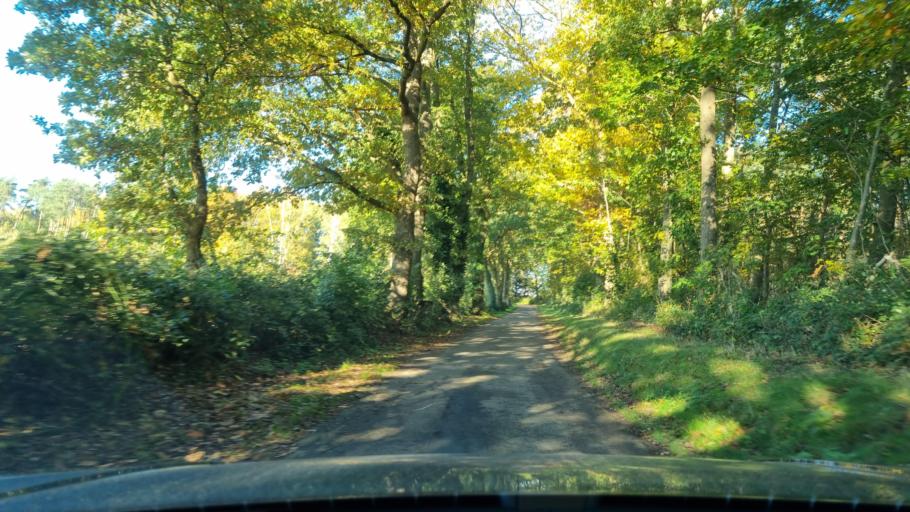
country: DE
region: North Rhine-Westphalia
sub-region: Regierungsbezirk Dusseldorf
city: Kranenburg
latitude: 51.7732
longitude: 6.0631
